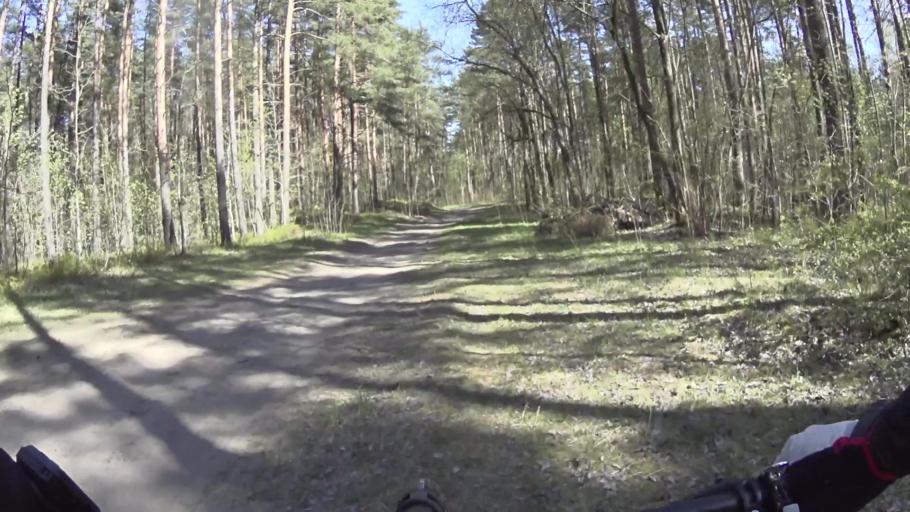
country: LV
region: Riga
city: Bolderaja
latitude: 56.9807
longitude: 24.0130
